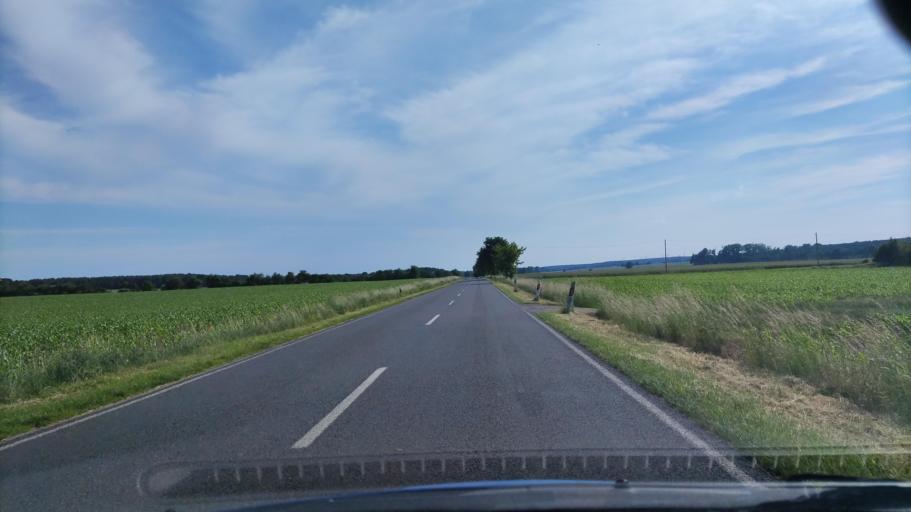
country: DE
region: Saxony-Anhalt
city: Klotze
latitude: 52.6610
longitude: 11.2024
